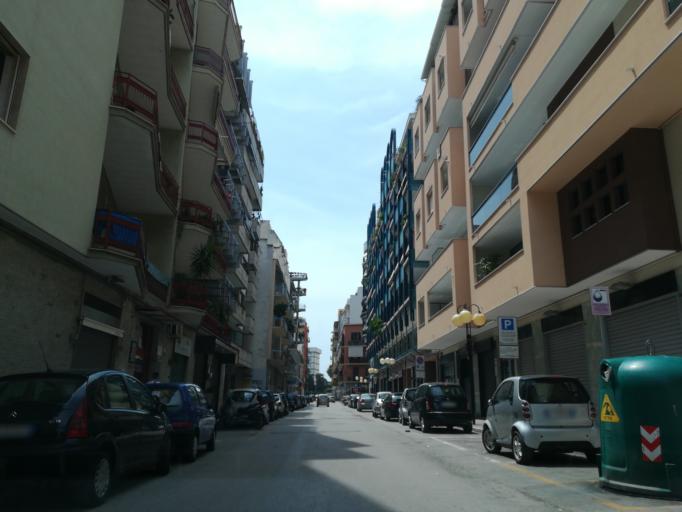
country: IT
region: Apulia
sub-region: Provincia di Barletta - Andria - Trani
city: Barletta
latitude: 41.3181
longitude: 16.2829
